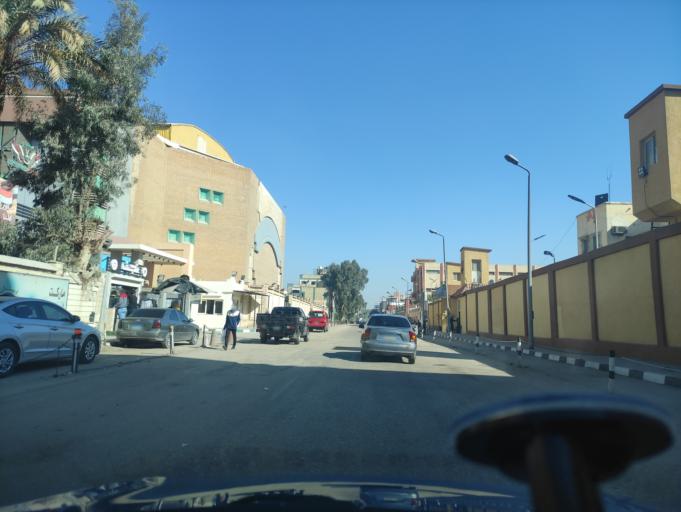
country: EG
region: Muhafazat al Qahirah
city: Cairo
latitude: 30.0529
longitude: 31.2758
